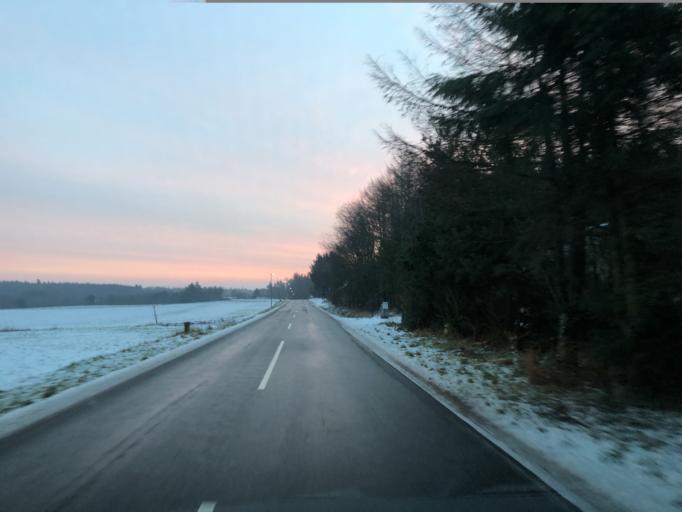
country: DK
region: Central Jutland
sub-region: Holstebro Kommune
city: Ulfborg
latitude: 56.2013
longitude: 8.4254
